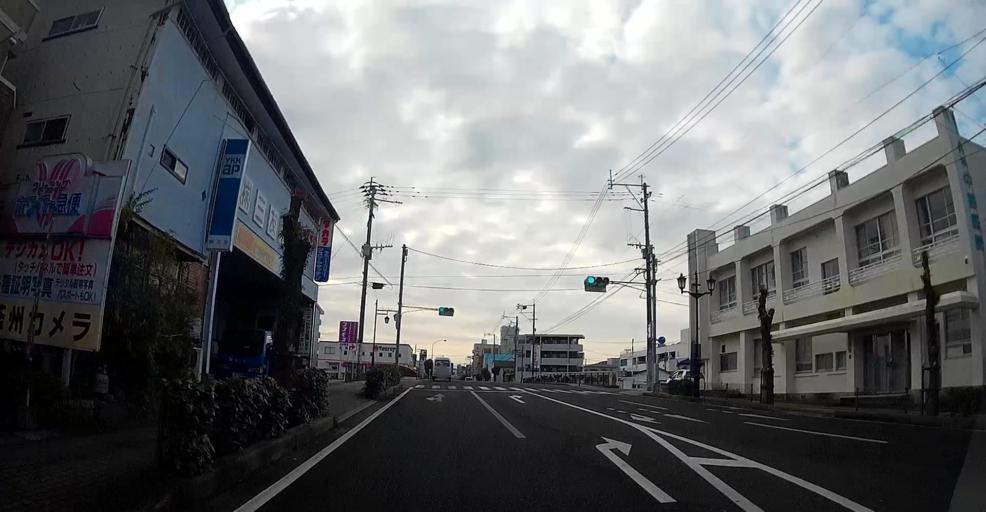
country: JP
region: Kumamoto
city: Hondo
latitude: 32.4574
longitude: 130.1931
